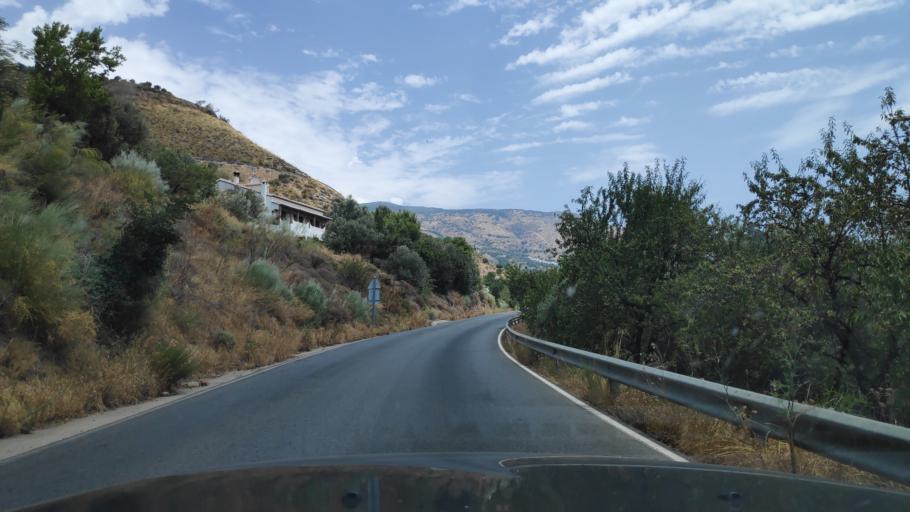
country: ES
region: Andalusia
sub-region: Provincia de Granada
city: Orjiva
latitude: 36.9103
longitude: -3.4304
